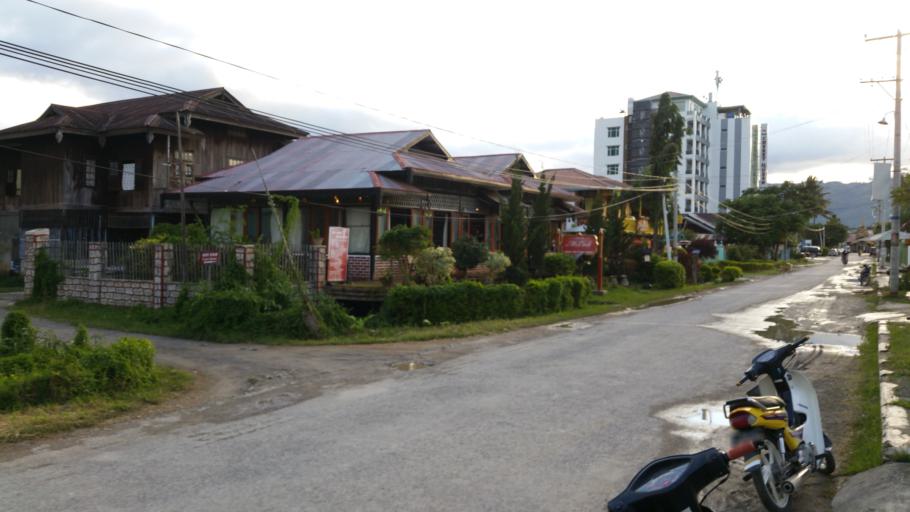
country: MM
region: Shan
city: Taunggyi
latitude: 20.6577
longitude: 96.9275
